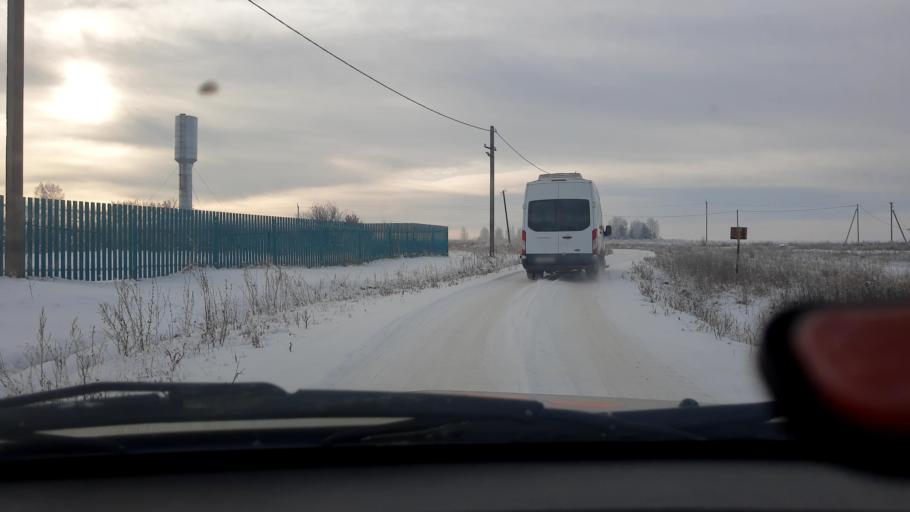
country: RU
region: Bashkortostan
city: Tolbazy
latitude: 54.3555
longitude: 55.8435
